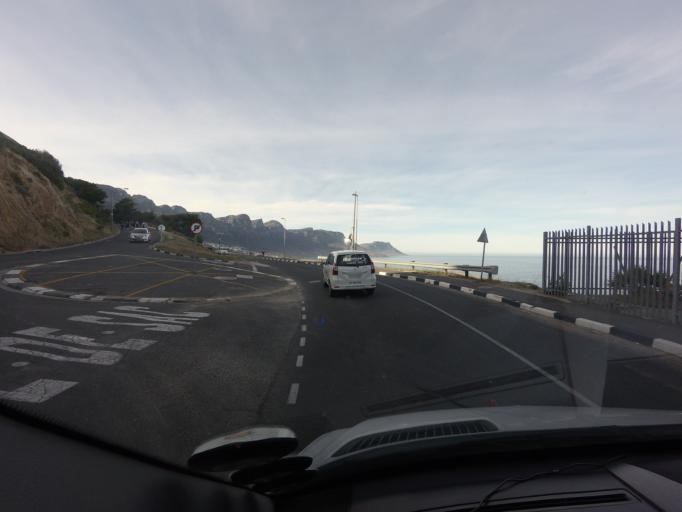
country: ZA
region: Western Cape
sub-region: City of Cape Town
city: Cape Town
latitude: -33.9300
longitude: 18.3770
